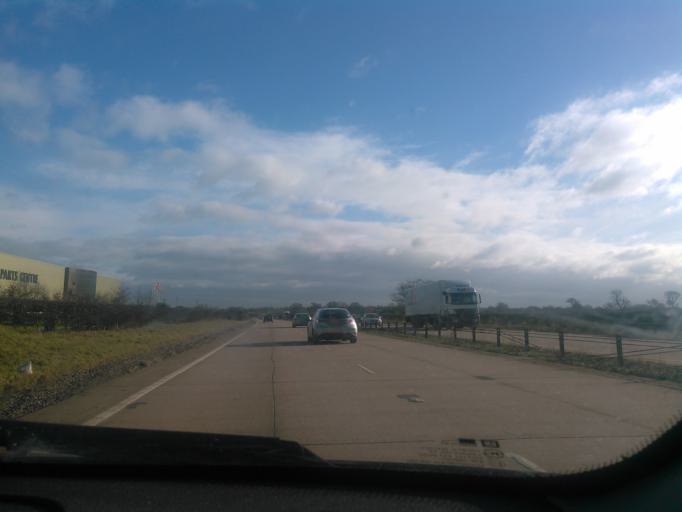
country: GB
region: England
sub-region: Staffordshire
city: Uttoxeter
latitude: 52.9150
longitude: -1.9036
